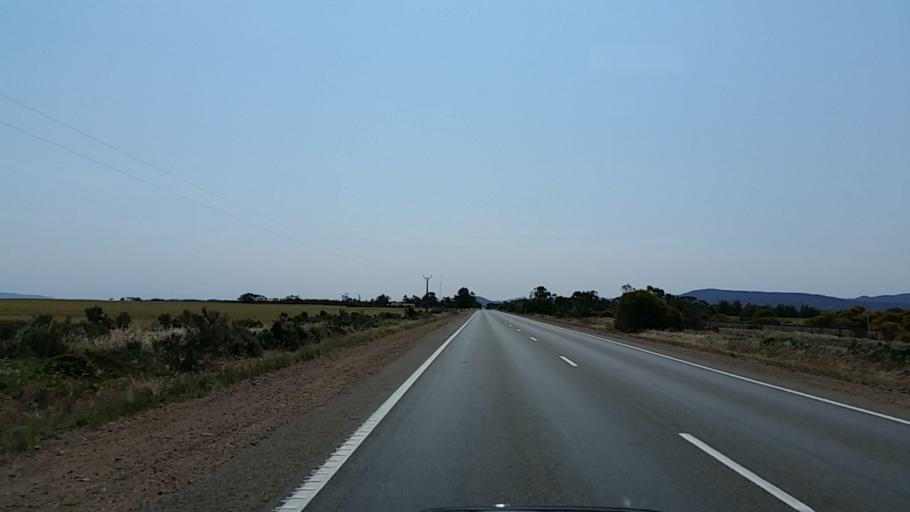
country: AU
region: South Australia
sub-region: Port Pirie City and Dists
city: Port Pirie
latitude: -32.9305
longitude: 137.9824
